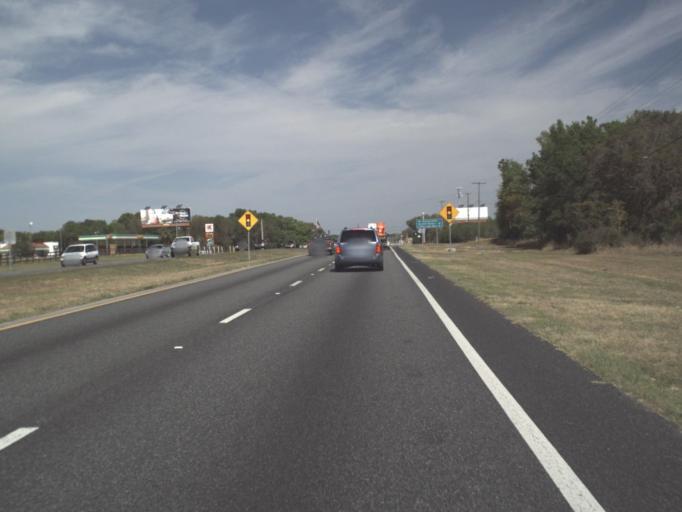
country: US
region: Florida
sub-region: Marion County
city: Belleview
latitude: 29.0052
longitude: -82.0042
